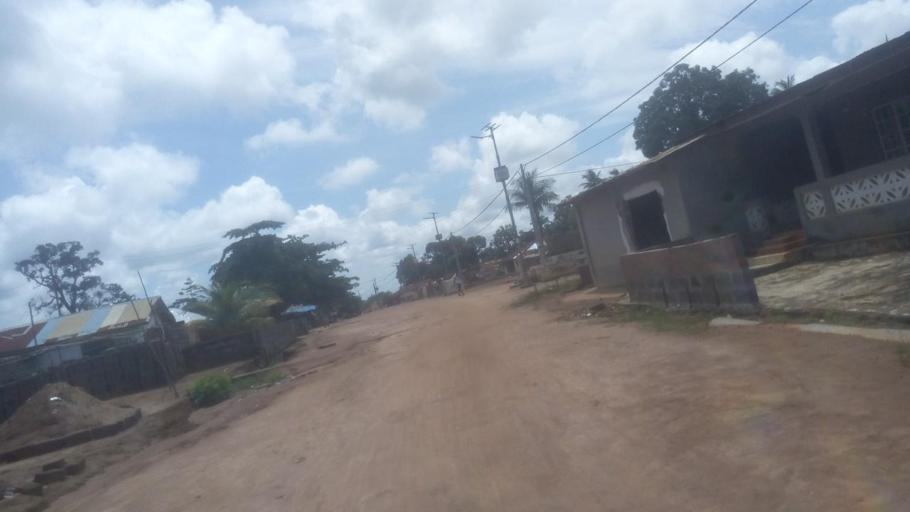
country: SL
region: Northern Province
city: Masoyila
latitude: 8.6062
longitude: -13.1974
